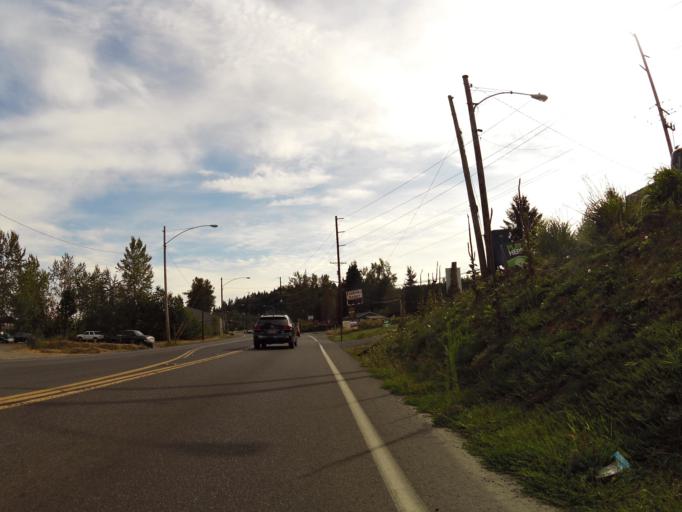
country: US
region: Washington
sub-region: Cowlitz County
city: West Side Highway
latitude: 46.1665
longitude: -122.9159
